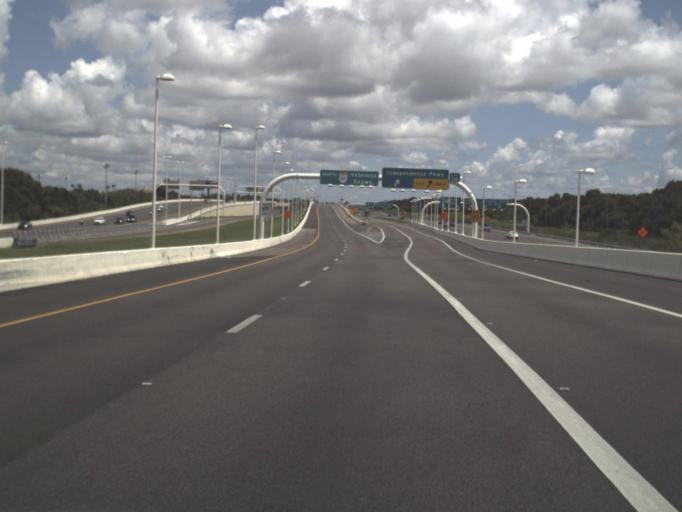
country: US
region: Florida
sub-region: Hillsborough County
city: Town 'n' Country
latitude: 27.9712
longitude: -82.5465
